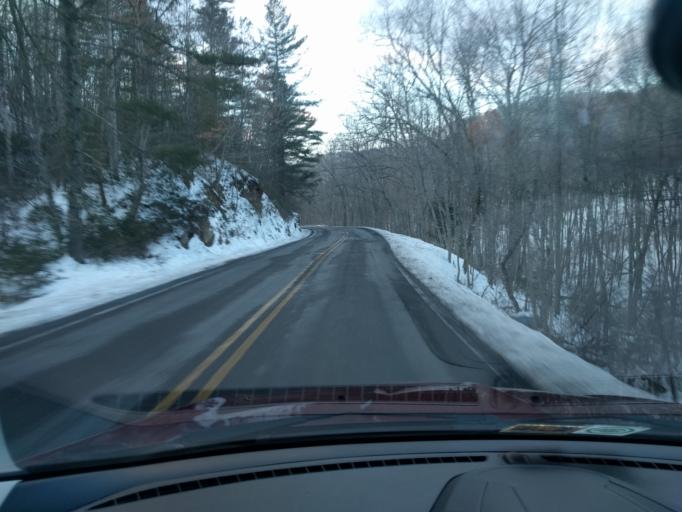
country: US
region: Virginia
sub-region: Bath County
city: Warm Springs
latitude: 38.0958
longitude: -79.8539
